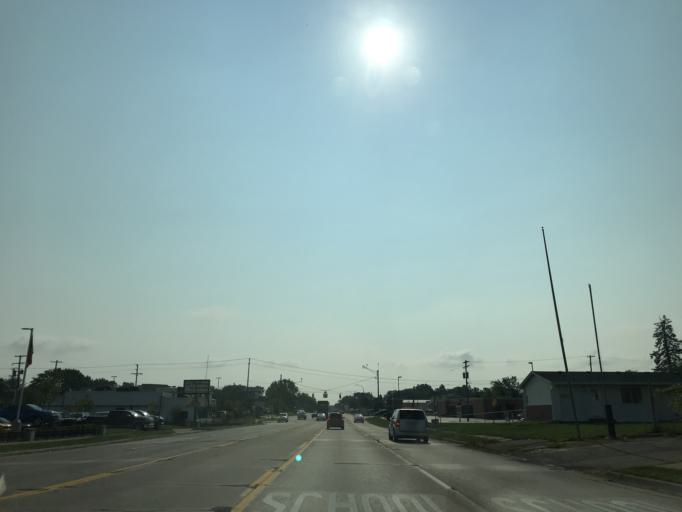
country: US
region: Michigan
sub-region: Washtenaw County
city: Ypsilanti
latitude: 42.2489
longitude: -83.6499
